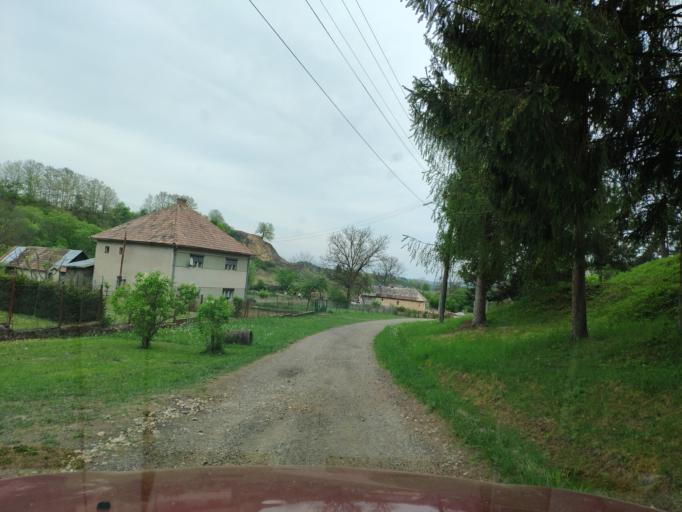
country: SK
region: Banskobystricky
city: Revuca
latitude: 48.5151
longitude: 20.1707
